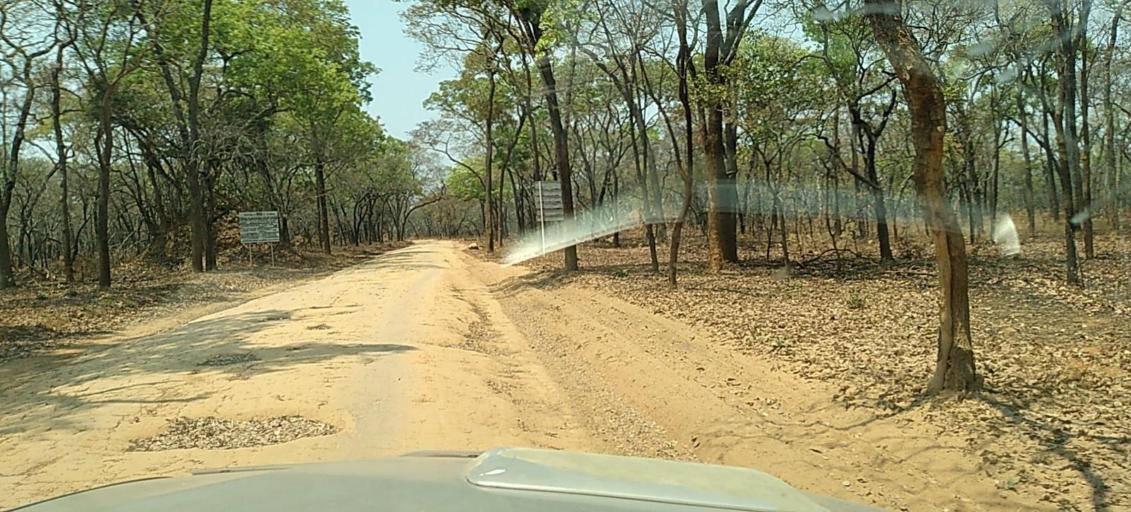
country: ZM
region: North-Western
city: Kasempa
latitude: -13.6074
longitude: 26.1799
